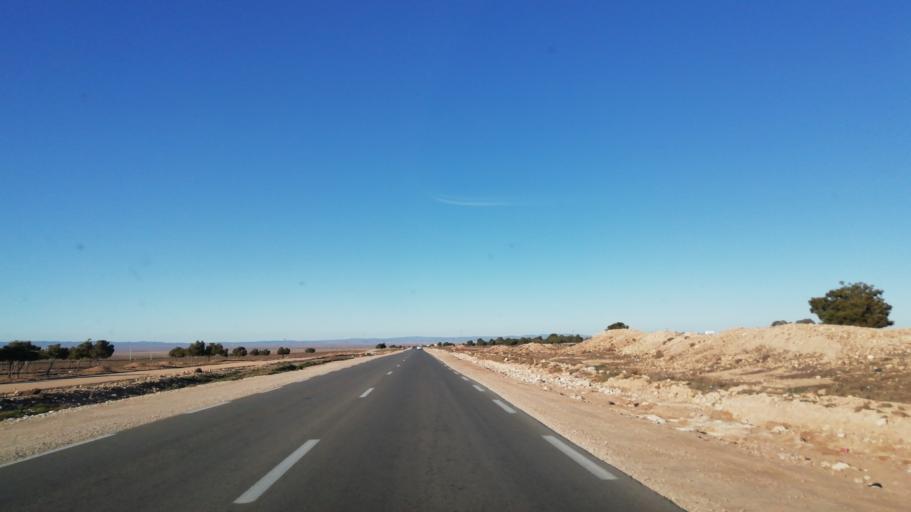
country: DZ
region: Tlemcen
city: Sebdou
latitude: 34.2941
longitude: -1.2604
